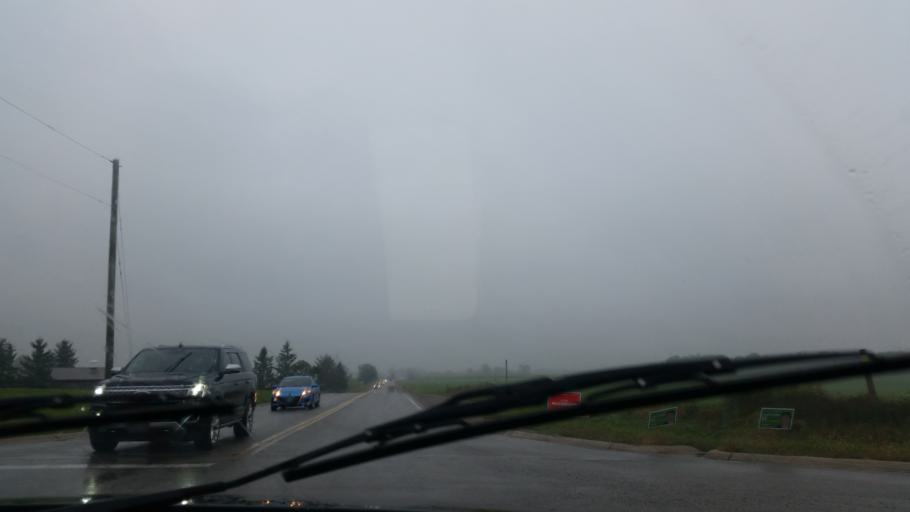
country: CA
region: Ontario
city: London
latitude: 43.0892
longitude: -81.3472
